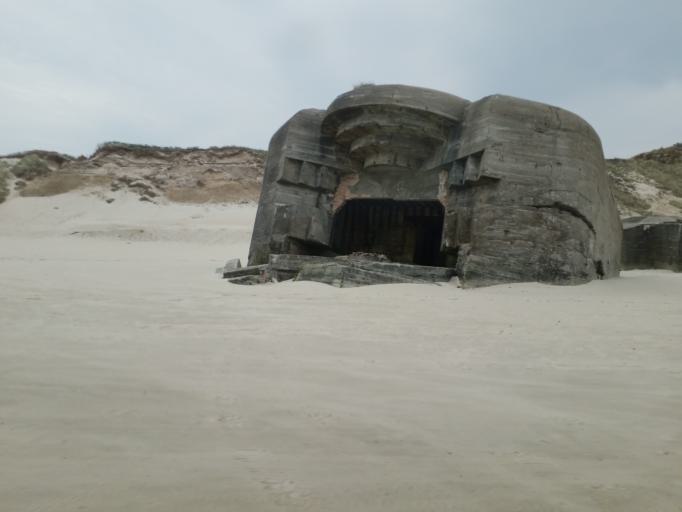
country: DK
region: North Denmark
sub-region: Jammerbugt Kommune
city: Pandrup
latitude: 57.3814
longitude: 9.7181
